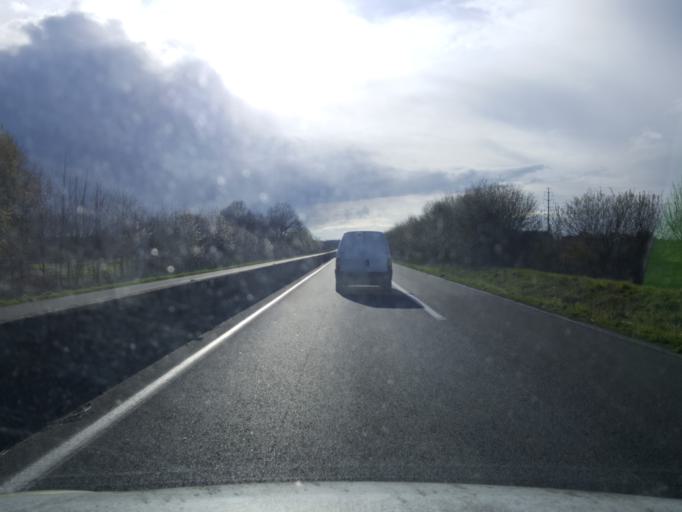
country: FR
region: Picardie
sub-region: Departement de l'Oise
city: Goincourt
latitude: 49.3835
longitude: 2.0423
